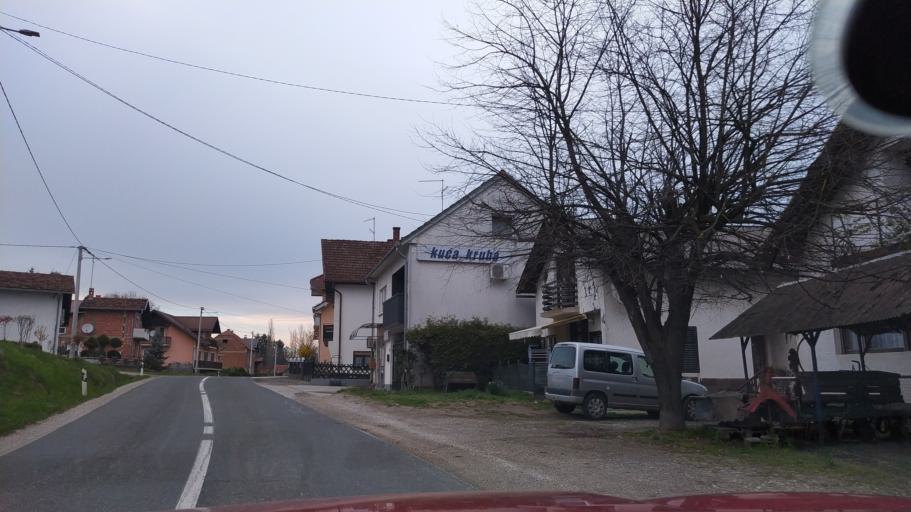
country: HR
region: Varazdinska
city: Ludbreg
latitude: 46.2282
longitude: 16.5454
